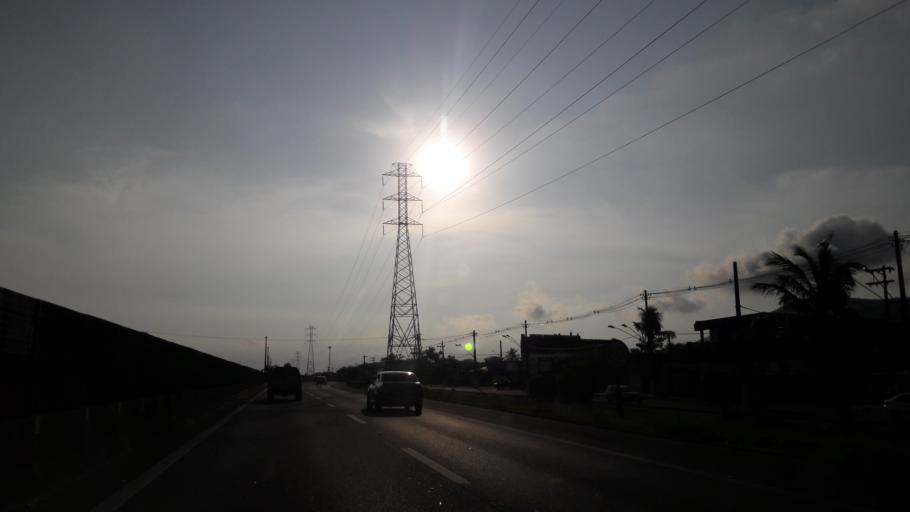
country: BR
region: Sao Paulo
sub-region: Itanhaem
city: Itanhaem
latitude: -24.1388
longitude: -46.7099
